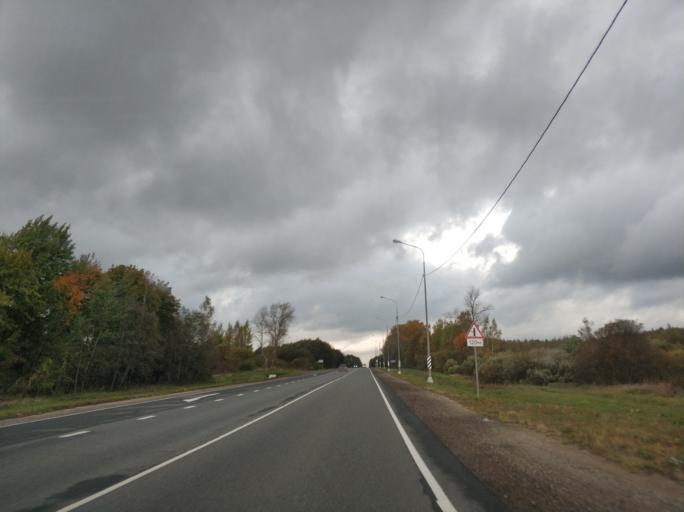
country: RU
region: Pskov
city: Ostrov
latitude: 57.1553
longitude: 28.4997
